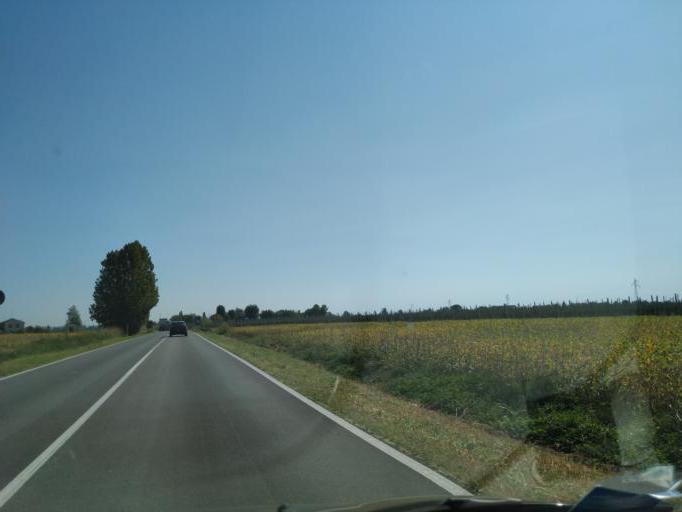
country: IT
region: Emilia-Romagna
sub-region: Provincia di Ferrara
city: Copparo
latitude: 44.8846
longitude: 11.8256
